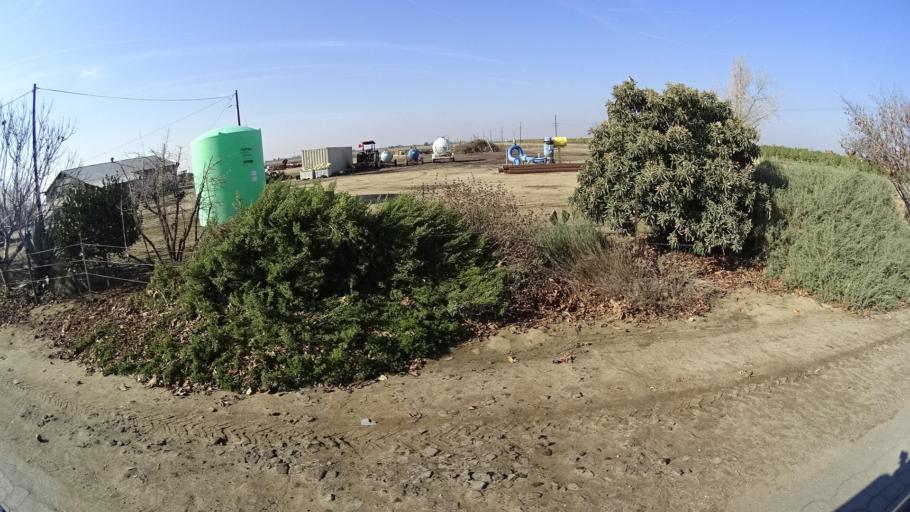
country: US
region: California
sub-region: Kern County
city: Arvin
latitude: 35.2232
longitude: -118.8603
